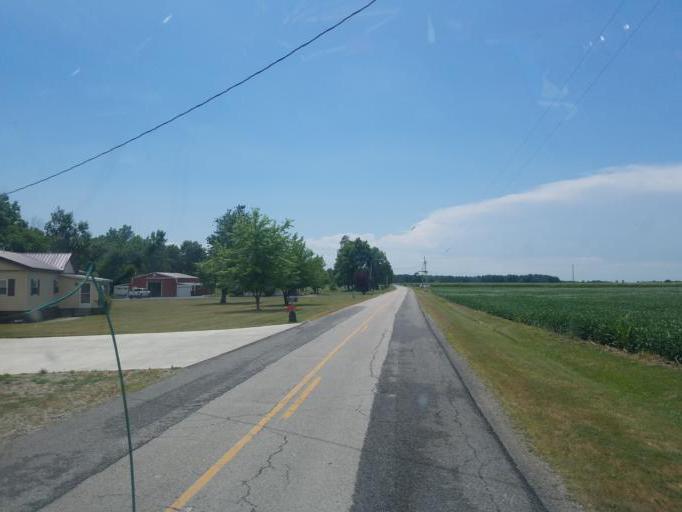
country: US
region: Ohio
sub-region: Paulding County
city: Antwerp
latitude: 41.1889
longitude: -84.7727
